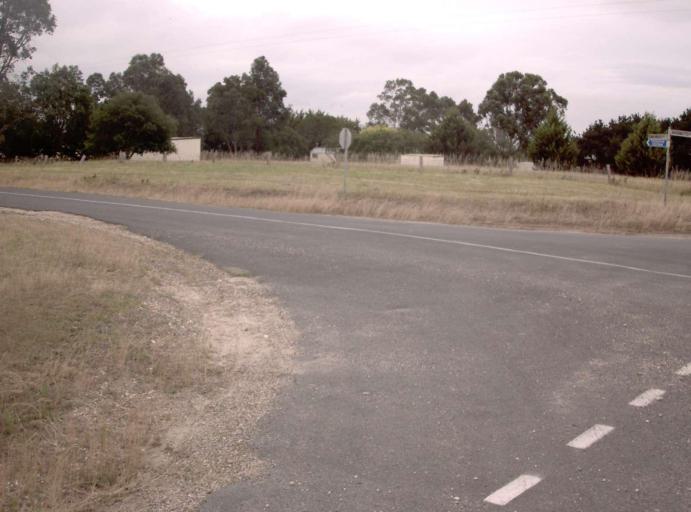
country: AU
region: Victoria
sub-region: East Gippsland
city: Bairnsdale
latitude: -37.8167
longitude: 147.4363
